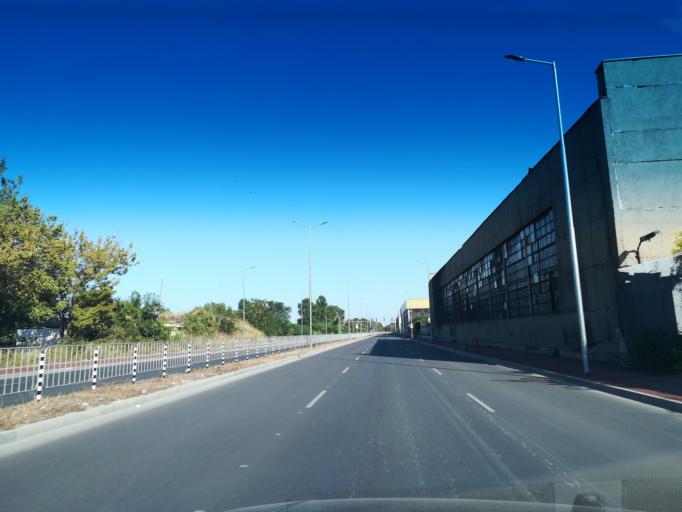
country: BG
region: Plovdiv
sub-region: Obshtina Plovdiv
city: Plovdiv
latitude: 42.1654
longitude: 24.7563
